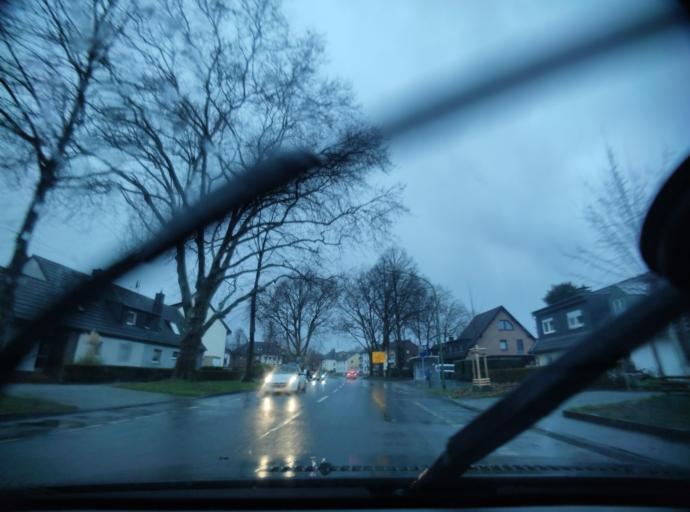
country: DE
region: North Rhine-Westphalia
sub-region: Regierungsbezirk Dusseldorf
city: Essen
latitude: 51.4854
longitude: 7.0239
